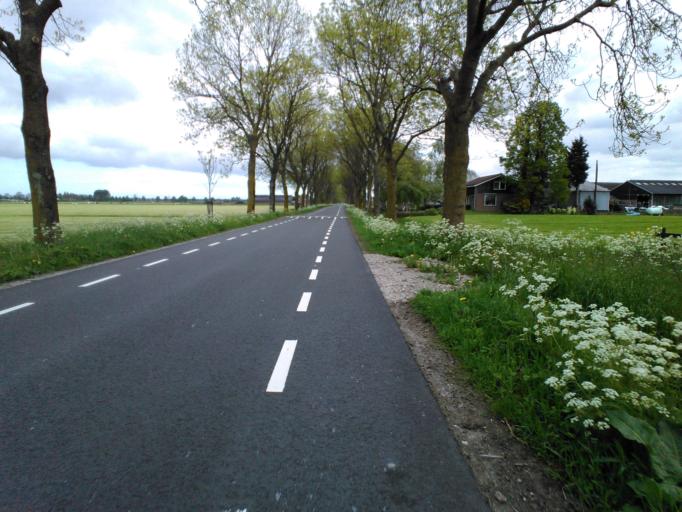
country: NL
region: South Holland
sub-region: Bodegraven-Reeuwijk
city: Bodegraven
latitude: 52.0871
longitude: 4.7210
